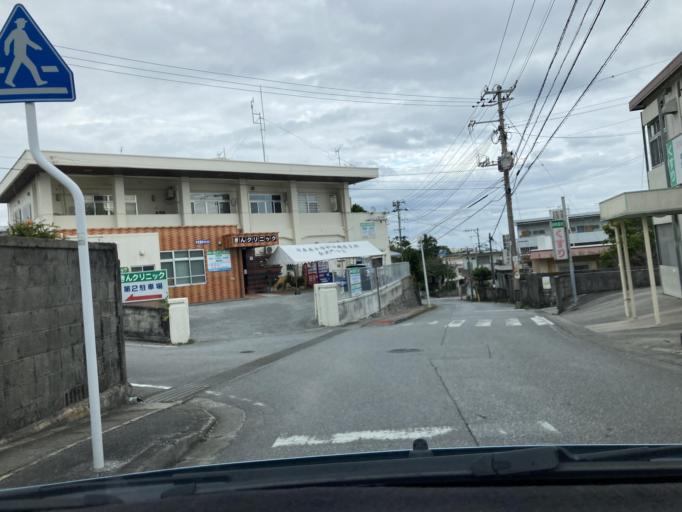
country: JP
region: Okinawa
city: Ishikawa
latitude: 26.4556
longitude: 127.9249
